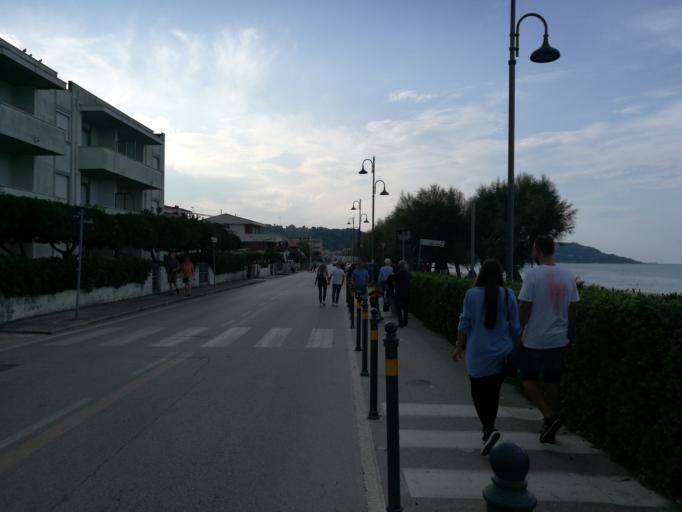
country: IT
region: Abruzzo
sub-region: Provincia di Chieti
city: Fossacesia
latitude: 42.2464
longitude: 14.5175
